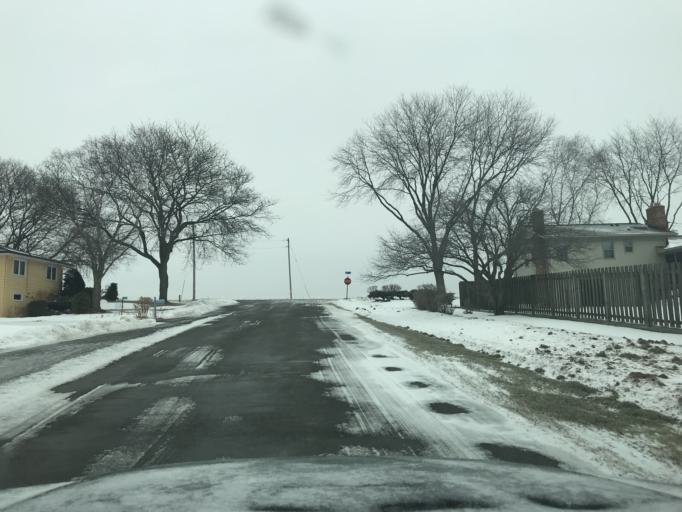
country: US
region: Wisconsin
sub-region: Dane County
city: Cottage Grove
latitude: 43.0951
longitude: -89.2305
